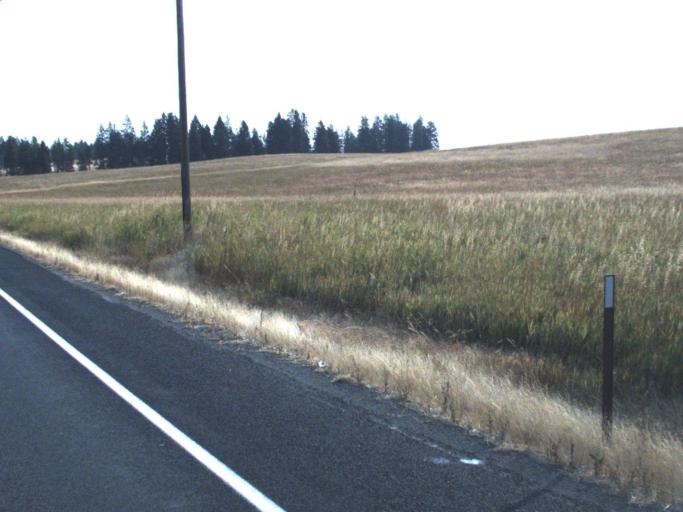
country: US
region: Idaho
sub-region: Benewah County
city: Plummer
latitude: 47.4403
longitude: -117.0840
